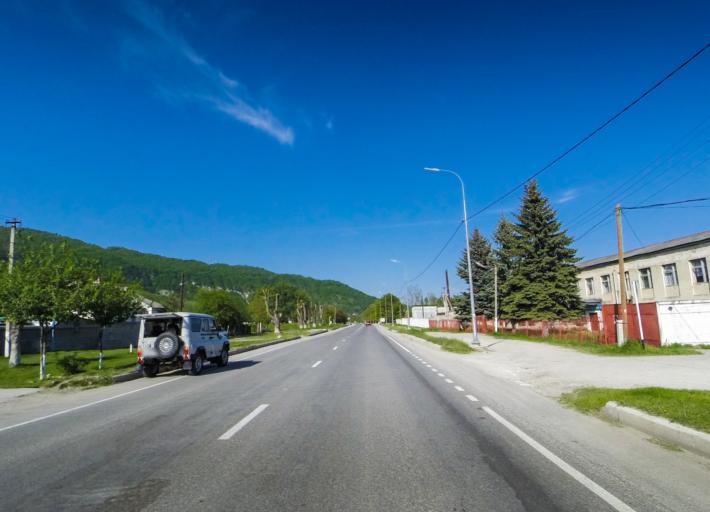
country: RU
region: Kabardino-Balkariya
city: Kashkhatau
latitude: 43.3239
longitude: 43.6227
